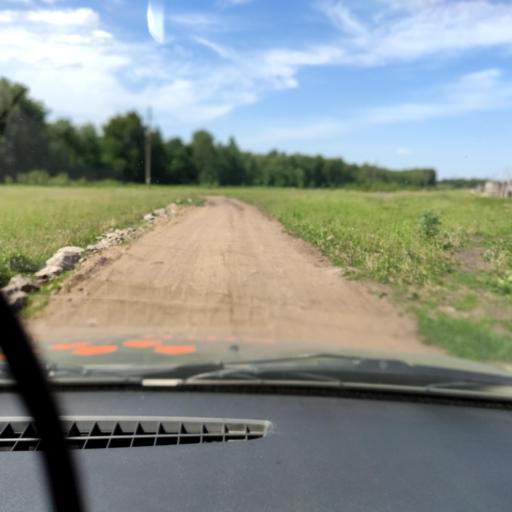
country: RU
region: Bashkortostan
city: Ufa
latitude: 54.6817
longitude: 56.0875
